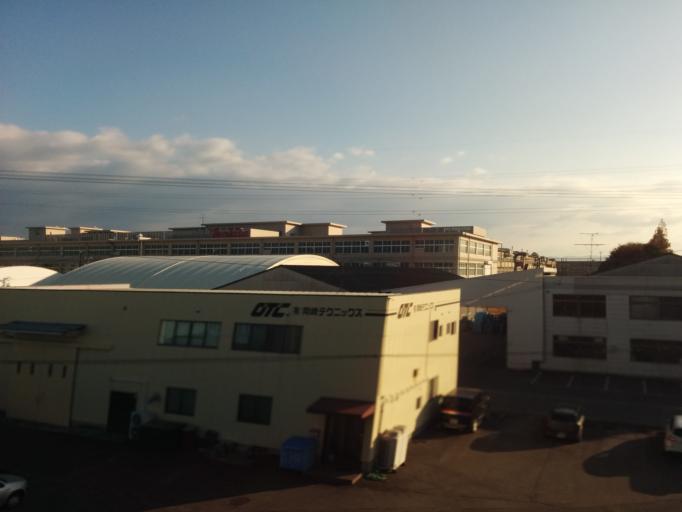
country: JP
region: Aichi
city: Anjo
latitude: 34.9095
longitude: 137.1152
